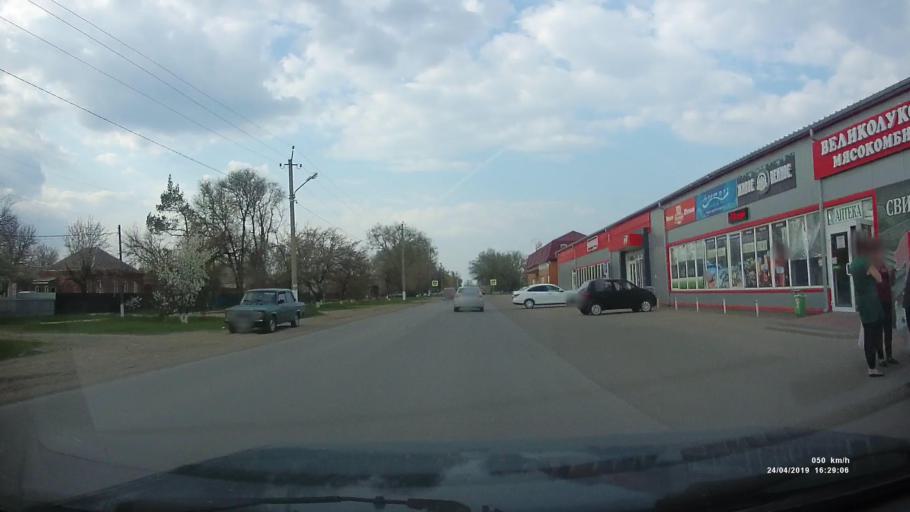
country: RU
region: Rostov
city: Orlovskiy
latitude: 46.8677
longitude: 42.0342
